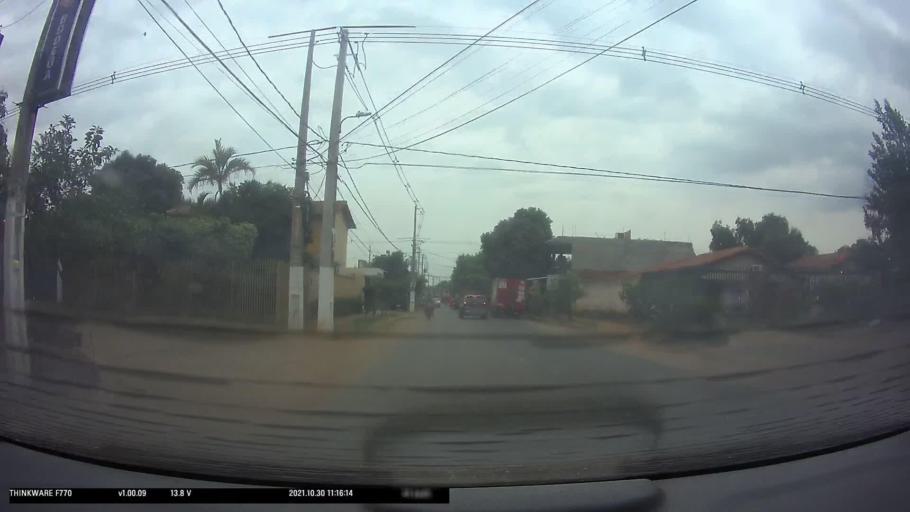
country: PY
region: Central
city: Fernando de la Mora
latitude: -25.3127
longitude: -57.5166
